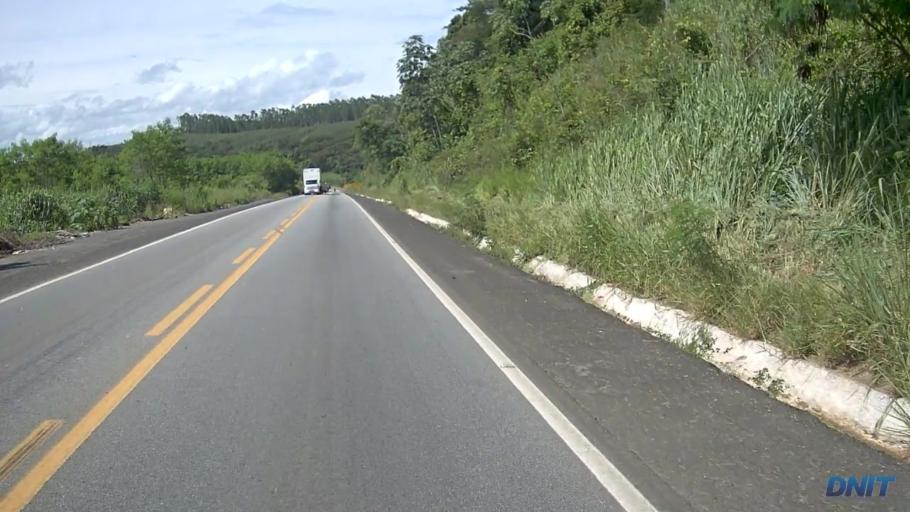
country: BR
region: Minas Gerais
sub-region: Ipaba
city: Ipaba
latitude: -19.4072
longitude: -42.4864
